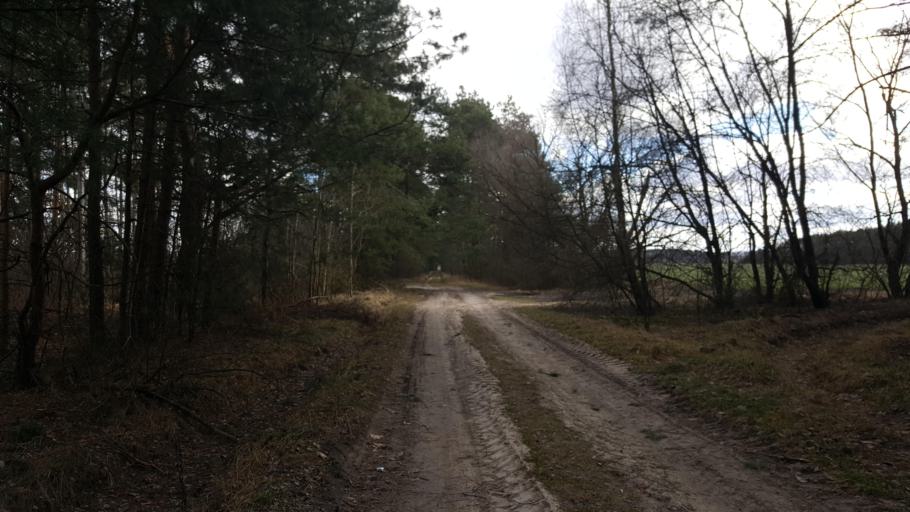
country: BY
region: Brest
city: Kamyanyets
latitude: 52.3936
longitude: 23.8701
